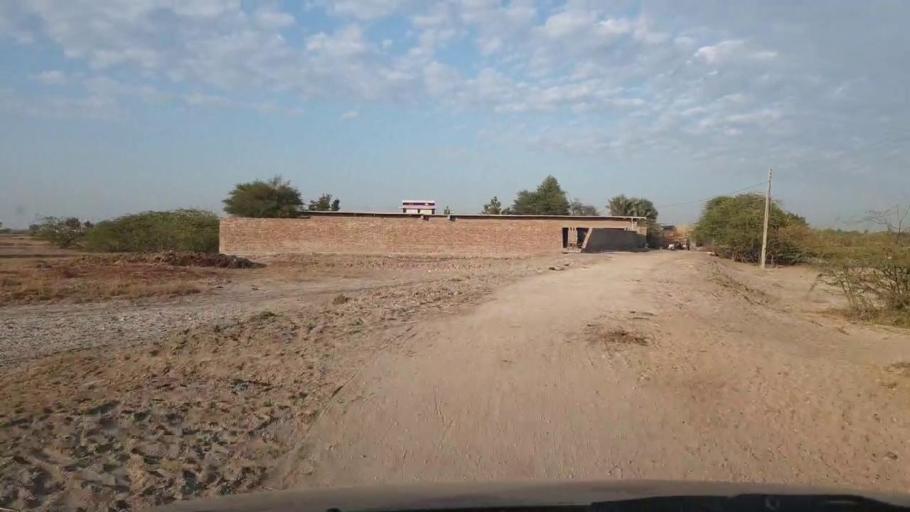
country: PK
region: Sindh
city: Sakrand
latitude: 26.0274
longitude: 68.3851
